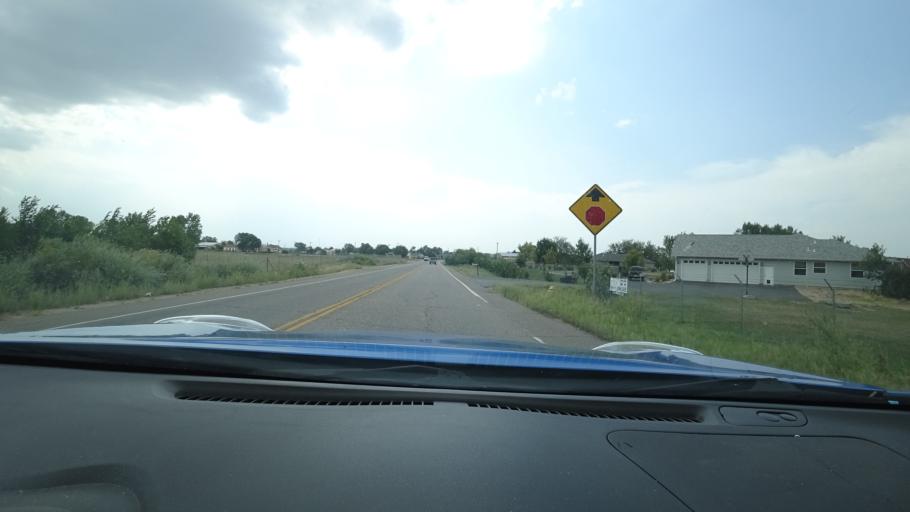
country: US
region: Colorado
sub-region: Adams County
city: Todd Creek
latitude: 39.9215
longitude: -104.8619
